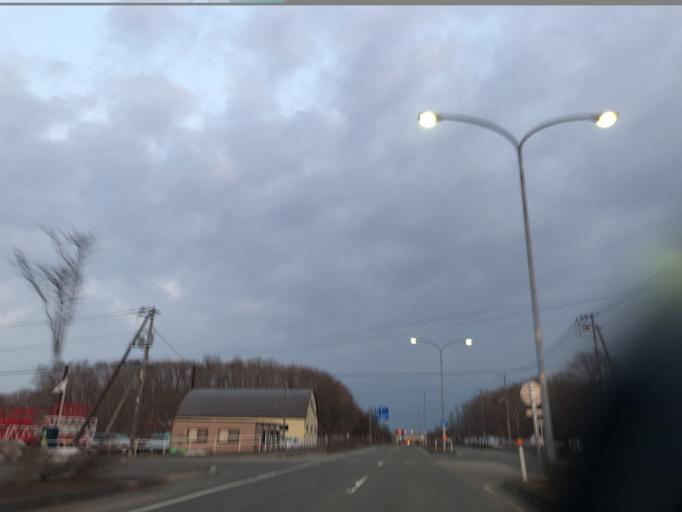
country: JP
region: Hokkaido
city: Chitose
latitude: 42.8204
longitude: 141.6755
